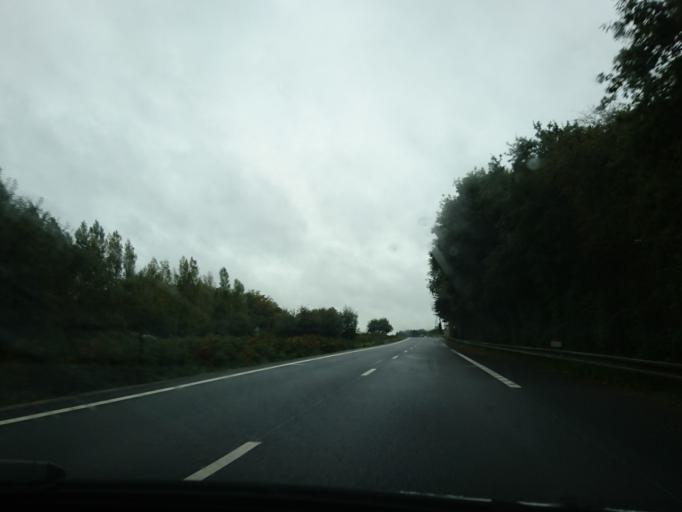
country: FR
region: Brittany
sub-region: Departement du Morbihan
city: Muzillac
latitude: 47.5623
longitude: -2.5064
